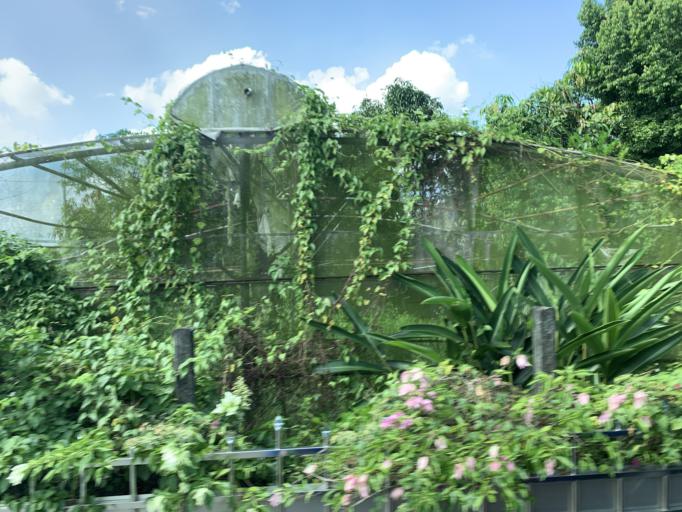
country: TW
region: Taiwan
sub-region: Pingtung
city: Pingtung
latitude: 22.8998
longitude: 120.5175
